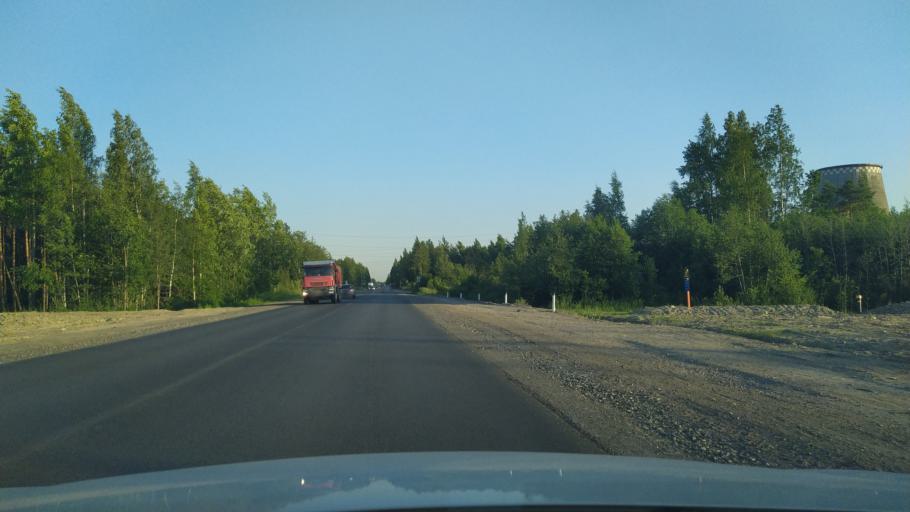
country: RU
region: Leningrad
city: Novoye Devyatkino
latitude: 60.0804
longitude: 30.4966
